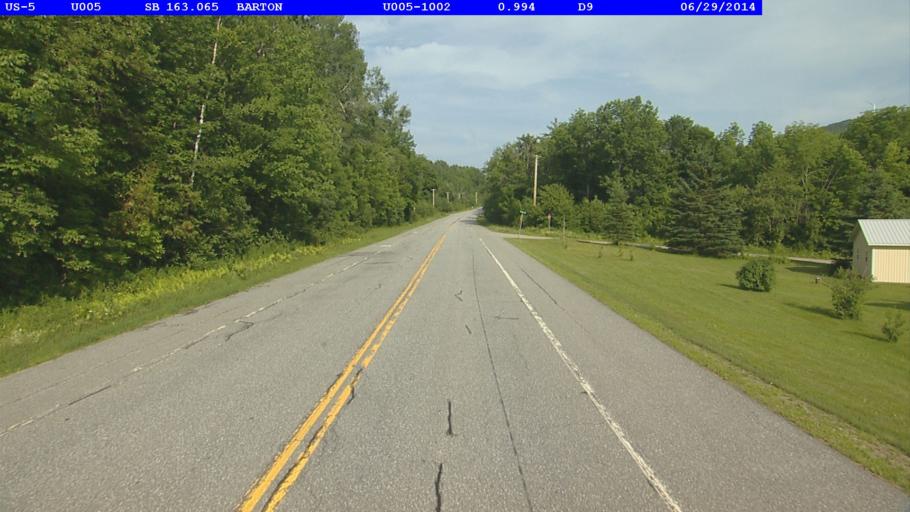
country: US
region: Vermont
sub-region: Caledonia County
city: Lyndonville
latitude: 44.7056
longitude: -72.1137
